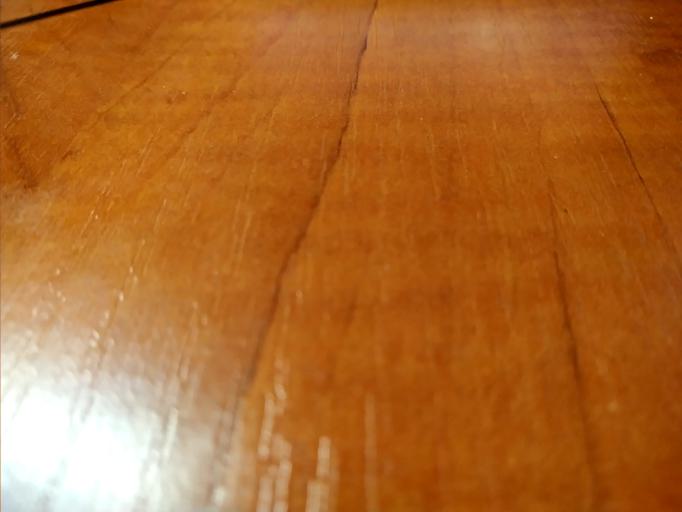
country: RU
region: Tverskaya
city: Spirovo
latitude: 57.3750
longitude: 34.9788
